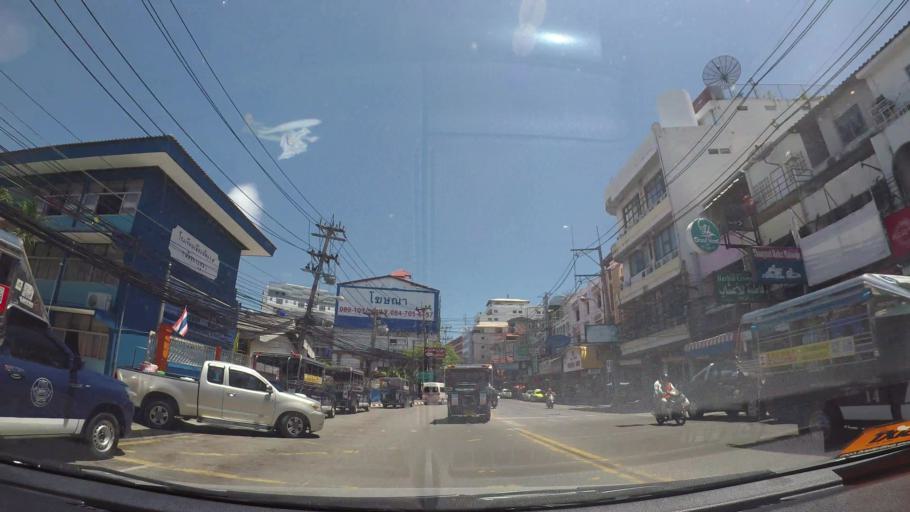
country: TH
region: Chon Buri
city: Phatthaya
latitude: 12.9257
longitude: 100.8748
